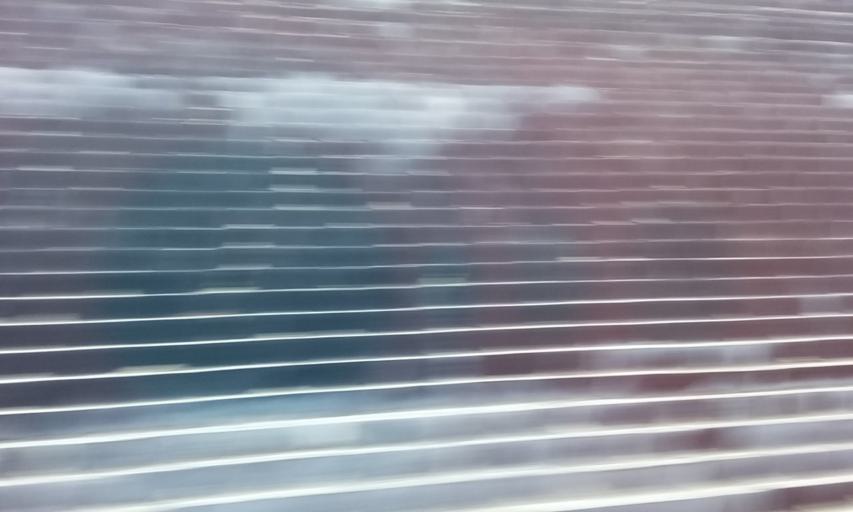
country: JP
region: Tochigi
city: Imaichi
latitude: 36.6555
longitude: 139.7115
